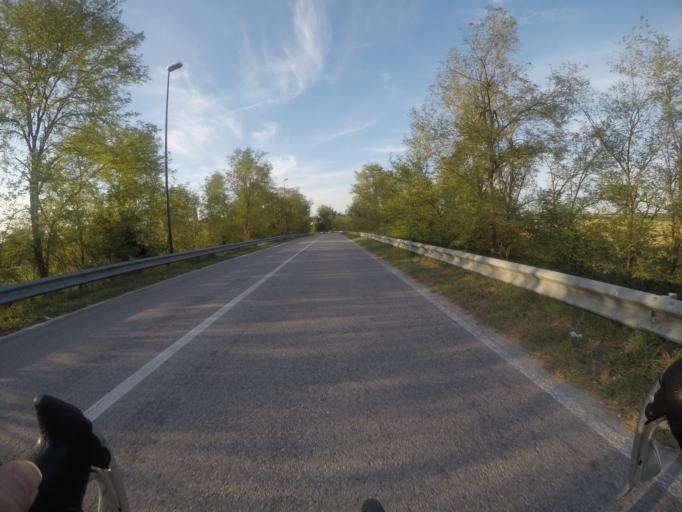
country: IT
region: Veneto
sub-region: Provincia di Rovigo
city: San Bellino
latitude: 45.0252
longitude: 11.5901
